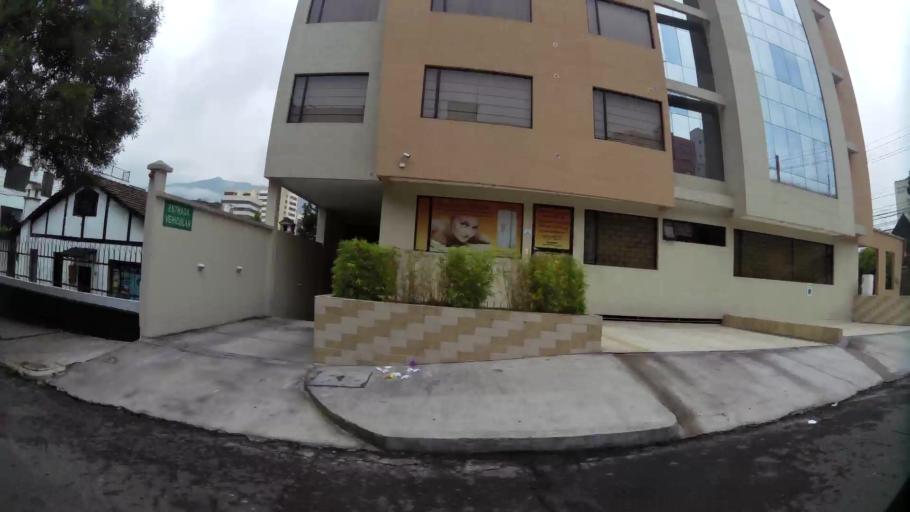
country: EC
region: Pichincha
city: Quito
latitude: -0.2069
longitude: -78.4828
